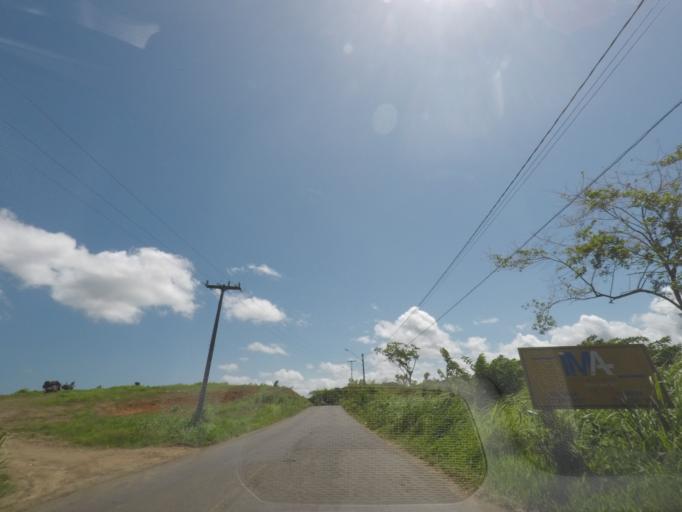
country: BR
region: Bahia
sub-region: Valenca
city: Valenca
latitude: -13.3813
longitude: -39.0750
